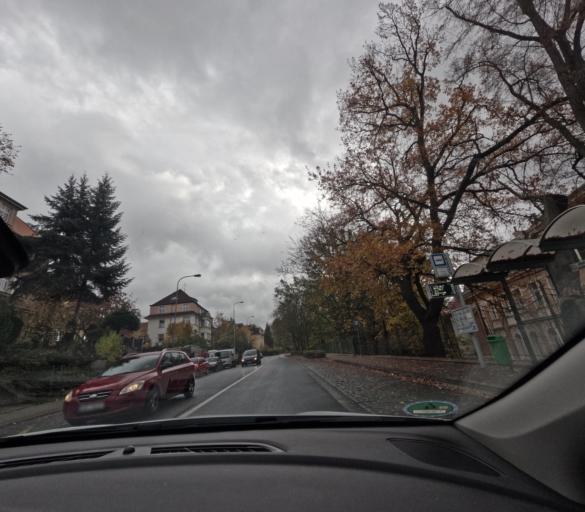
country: CZ
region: Karlovarsky
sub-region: Okres Karlovy Vary
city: Karlovy Vary
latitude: 50.2315
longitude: 12.8755
